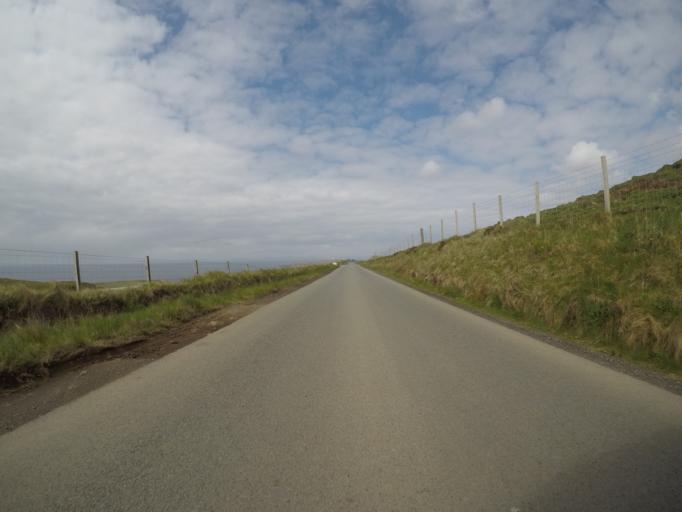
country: GB
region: Scotland
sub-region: Highland
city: Portree
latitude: 57.6002
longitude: -6.3767
